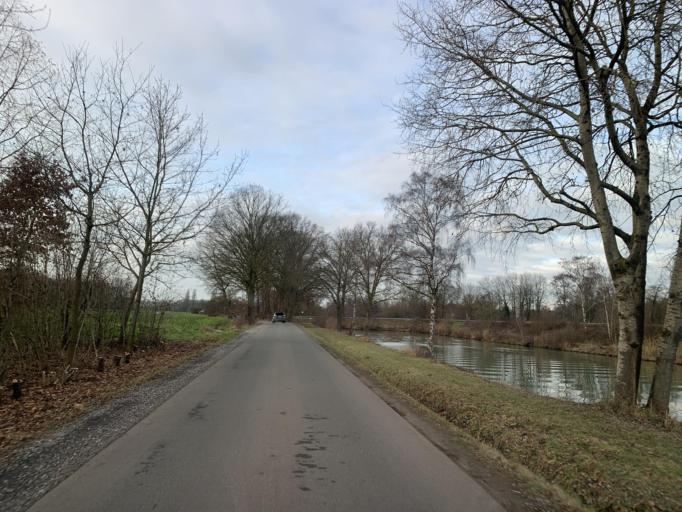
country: DE
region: North Rhine-Westphalia
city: Ludinghausen
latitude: 51.7794
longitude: 7.4056
